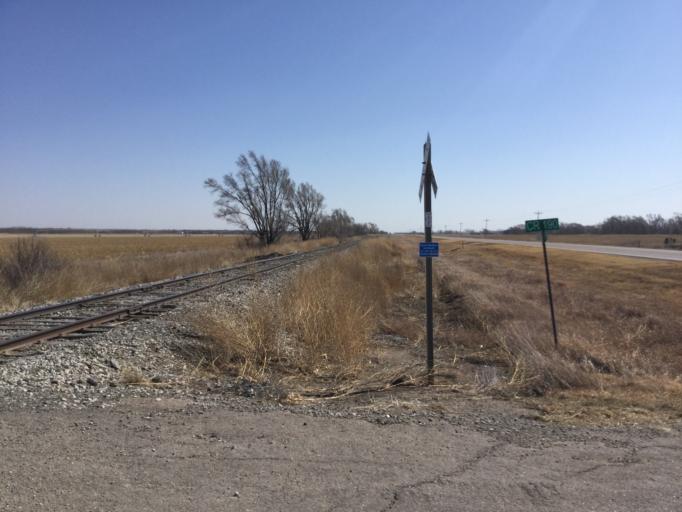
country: US
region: Kansas
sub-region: Rush County
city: La Crosse
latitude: 38.4725
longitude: -99.4194
